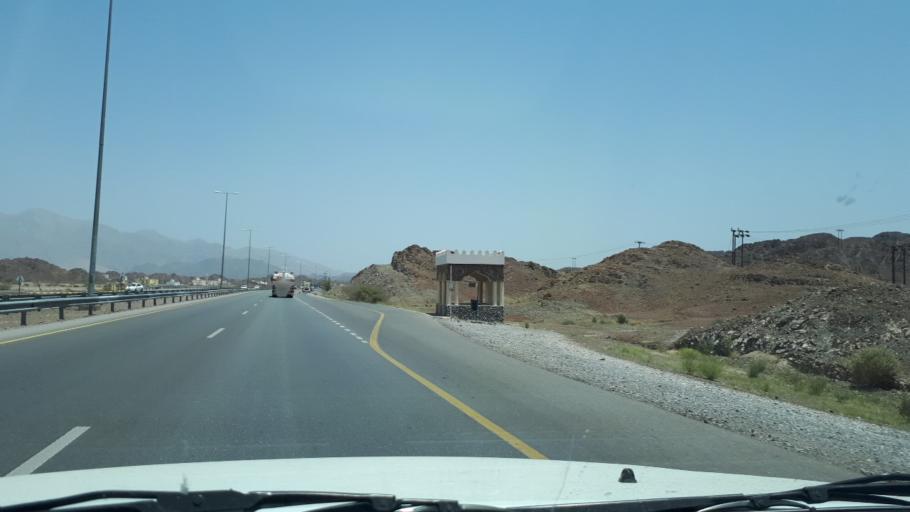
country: OM
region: Muhafazat ad Dakhiliyah
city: Sufalat Sama'il
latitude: 23.3190
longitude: 57.9585
